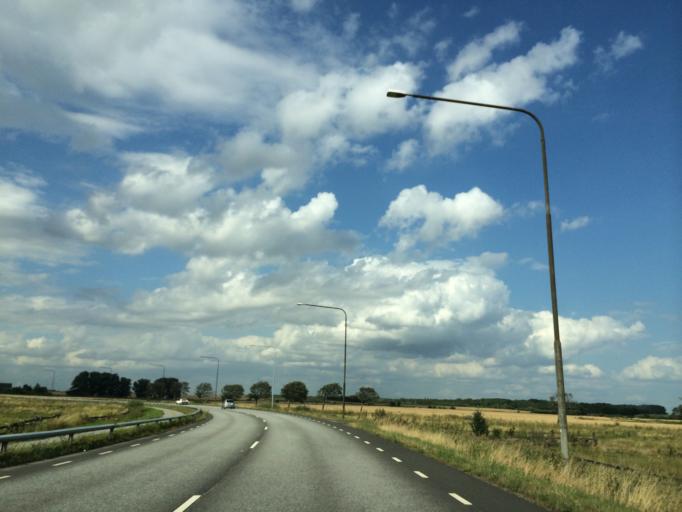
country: SE
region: Skane
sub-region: Burlovs Kommun
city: Arloev
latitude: 55.6434
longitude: 13.0588
